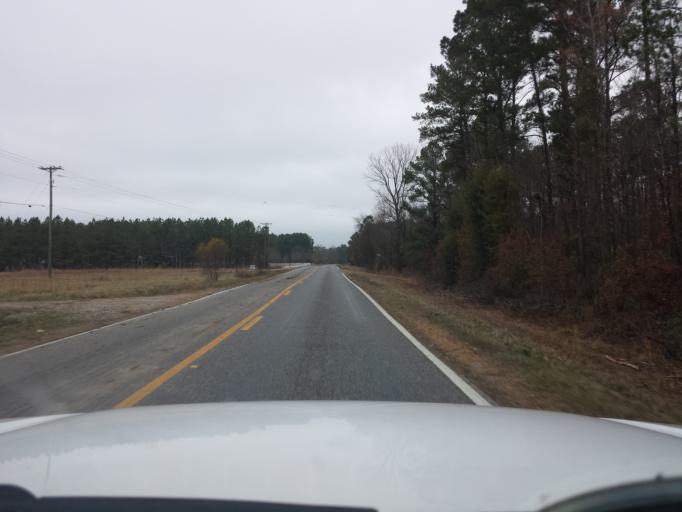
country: US
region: Mississippi
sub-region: Madison County
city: Canton
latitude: 32.4860
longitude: -89.9203
